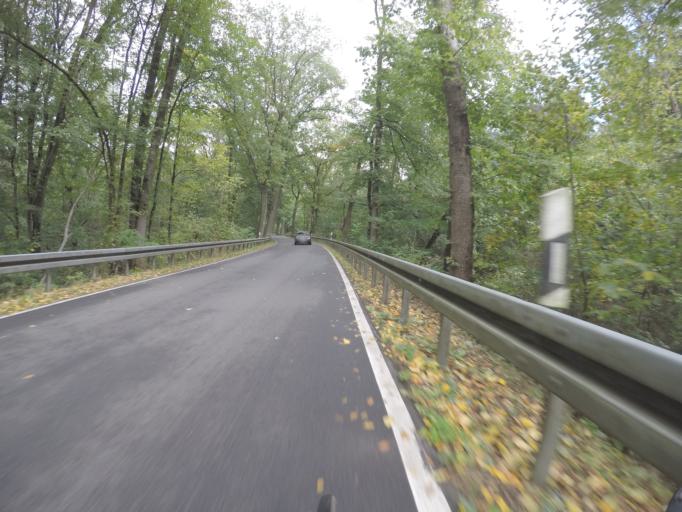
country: DE
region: Brandenburg
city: Strausberg
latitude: 52.6034
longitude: 13.8909
